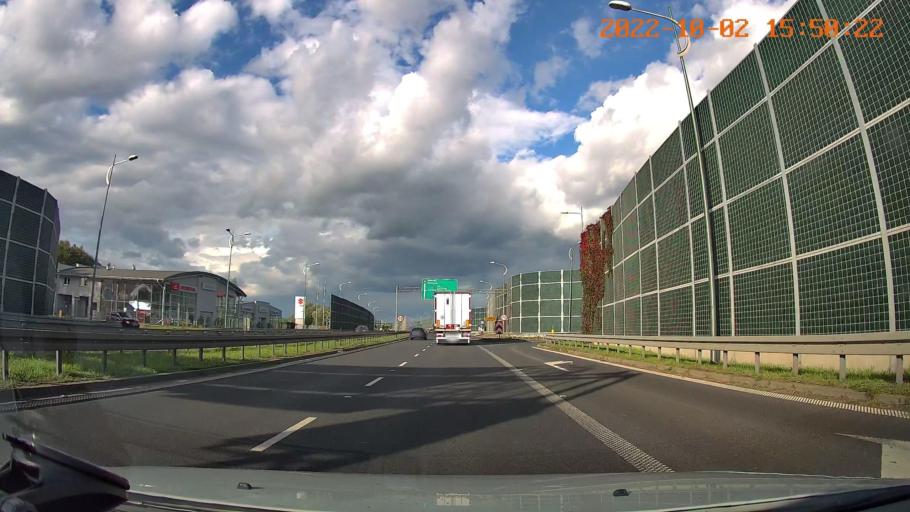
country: PL
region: Silesian Voivodeship
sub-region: Tychy
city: Cielmice
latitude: 50.1265
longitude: 19.0241
